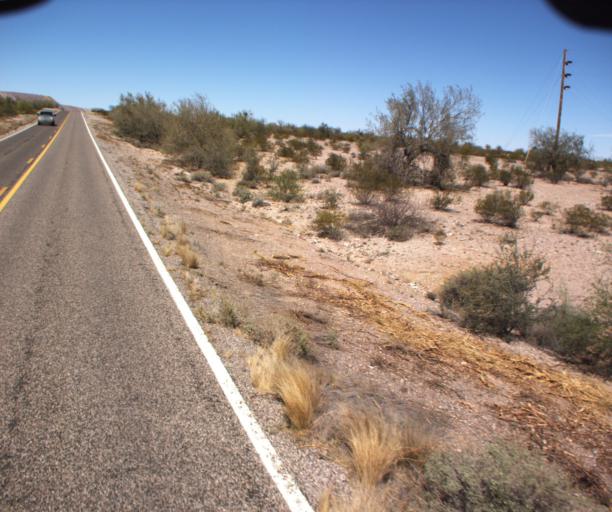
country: US
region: Arizona
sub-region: Pima County
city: Ajo
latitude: 32.3475
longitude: -112.8125
